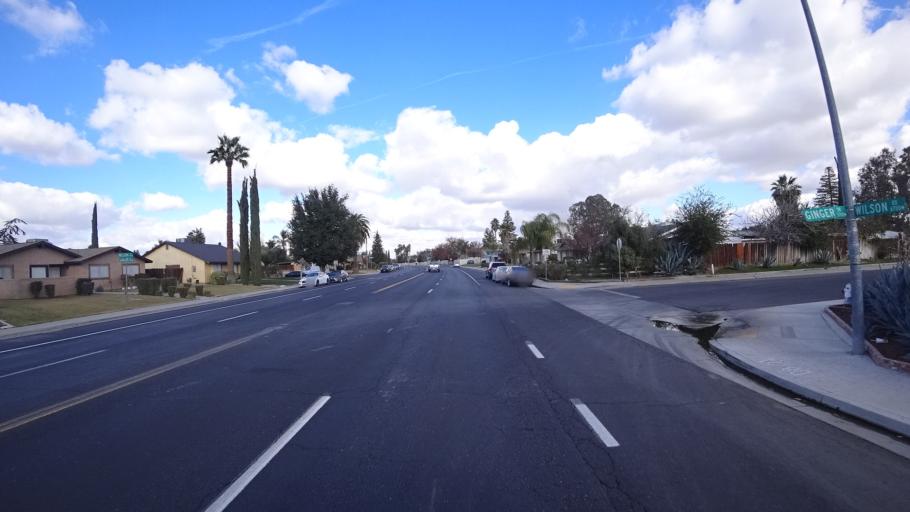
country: US
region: California
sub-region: Kern County
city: Bakersfield
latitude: 35.3204
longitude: -119.0681
